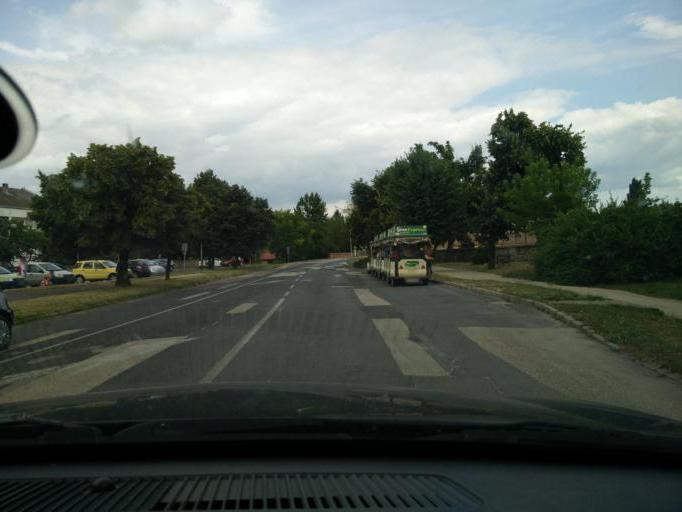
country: HU
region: Komarom-Esztergom
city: Tata
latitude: 47.6496
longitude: 18.3180
